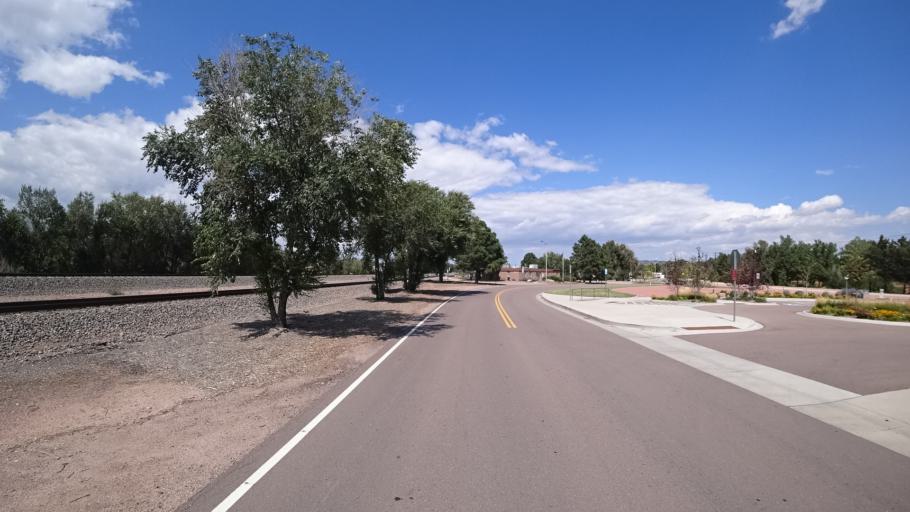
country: US
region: Colorado
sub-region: El Paso County
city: Colorado Springs
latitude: 38.8595
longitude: -104.8329
